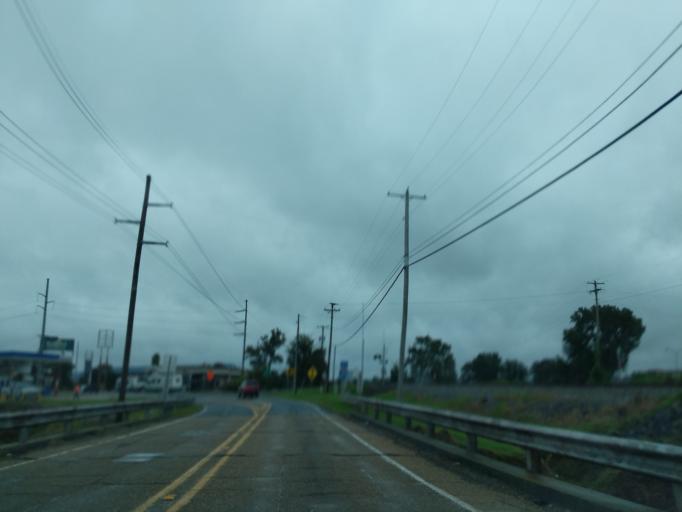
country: US
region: Louisiana
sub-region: Bossier Parish
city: Bossier City
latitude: 32.5264
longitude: -93.6763
